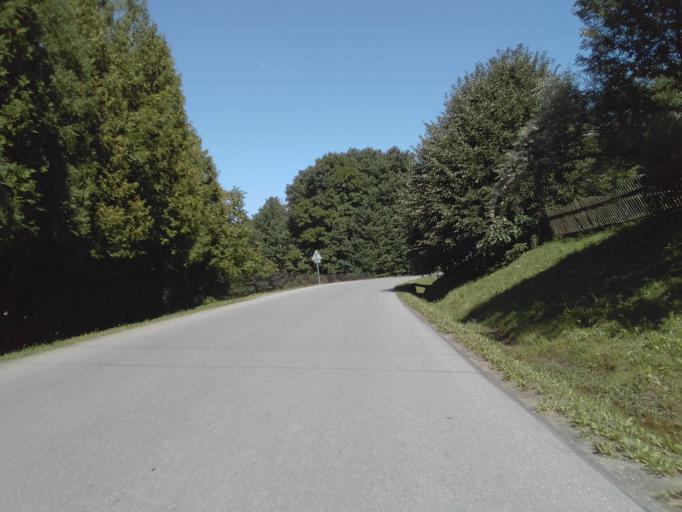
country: PL
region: Subcarpathian Voivodeship
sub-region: Powiat krosnienski
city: Chorkowka
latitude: 49.6579
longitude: 21.6098
